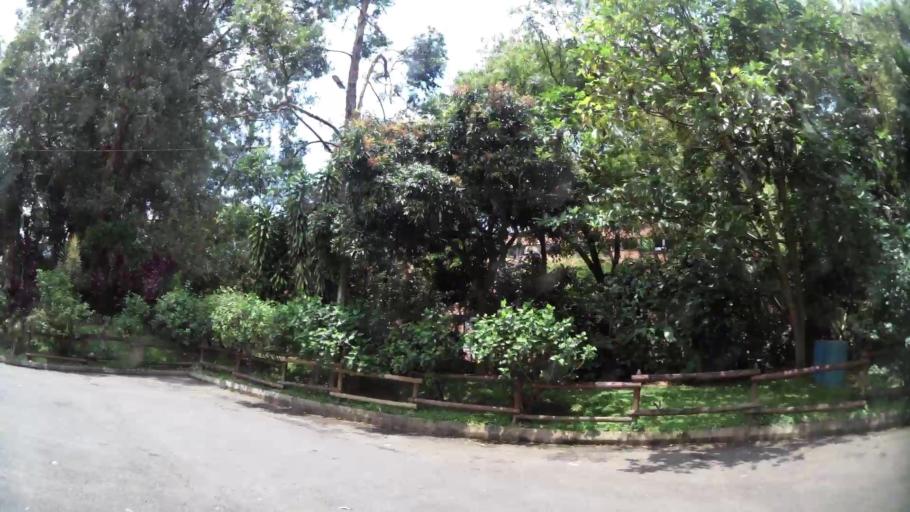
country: CO
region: Antioquia
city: Envigado
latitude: 6.1801
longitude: -75.5717
